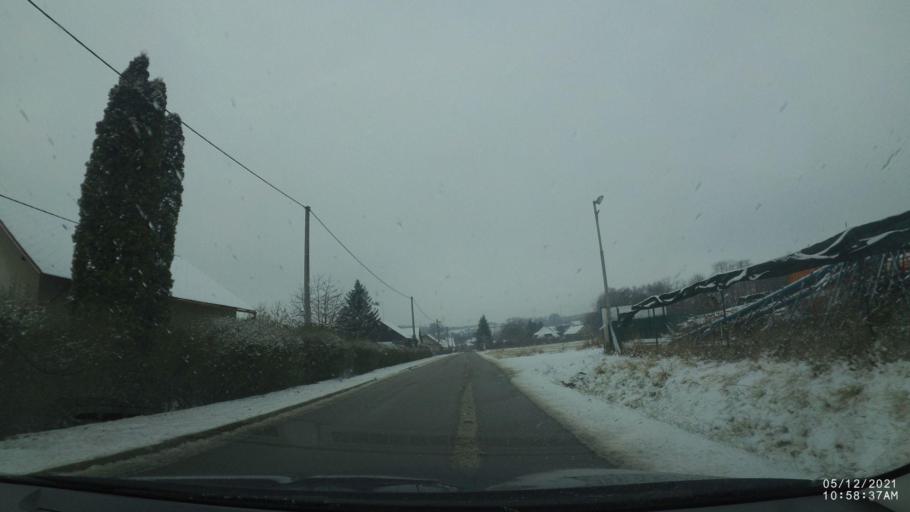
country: CZ
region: Kralovehradecky
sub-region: Okres Rychnov nad Kneznou
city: Rychnov nad Kneznou
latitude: 50.1637
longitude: 16.2445
